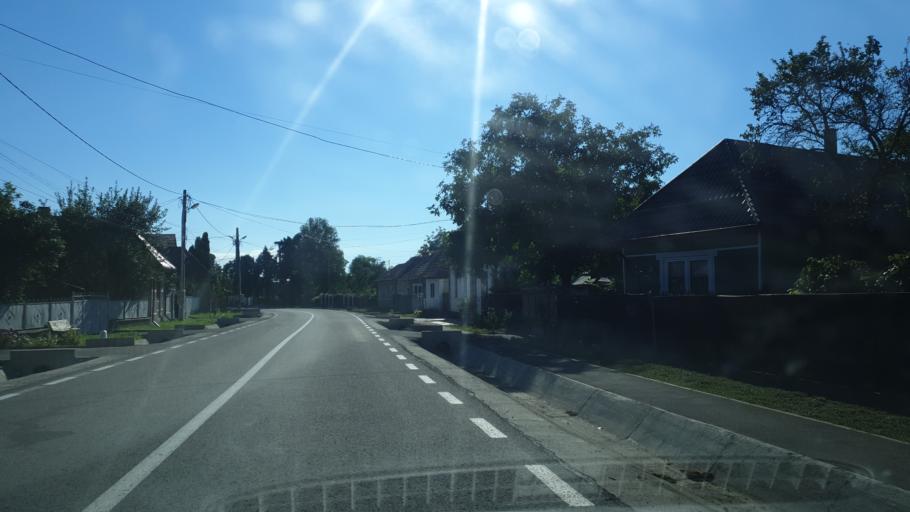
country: RO
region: Covasna
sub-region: Comuna Ilieni
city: Ilieni
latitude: 45.7797
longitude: 25.7552
